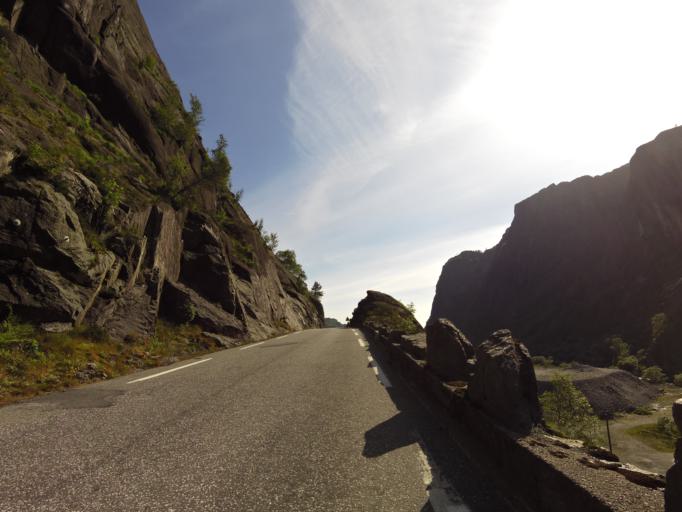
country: NO
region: Rogaland
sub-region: Sokndal
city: Hauge i Dalane
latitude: 58.3278
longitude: 6.3537
